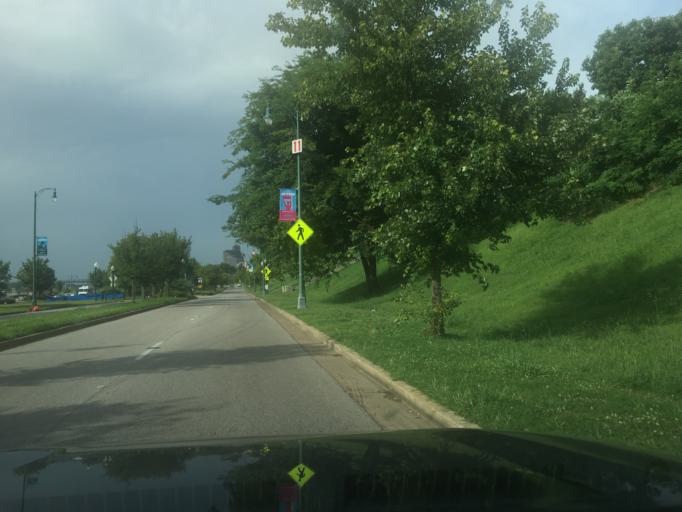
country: US
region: Tennessee
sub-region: Shelby County
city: Memphis
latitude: 35.1343
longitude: -90.0642
